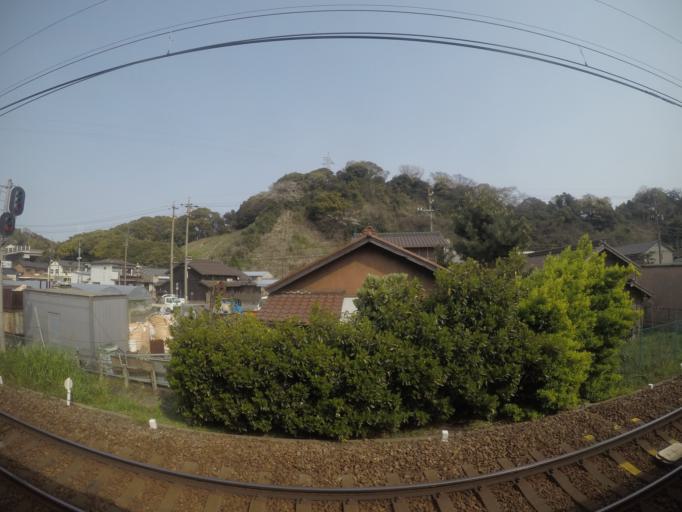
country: JP
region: Aichi
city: Obu
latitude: 35.0398
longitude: 136.9024
